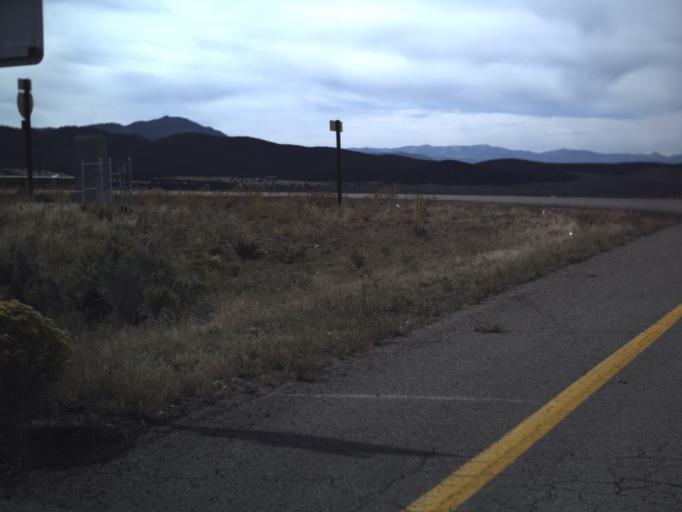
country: US
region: Utah
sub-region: Beaver County
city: Beaver
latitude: 38.1313
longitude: -112.6283
